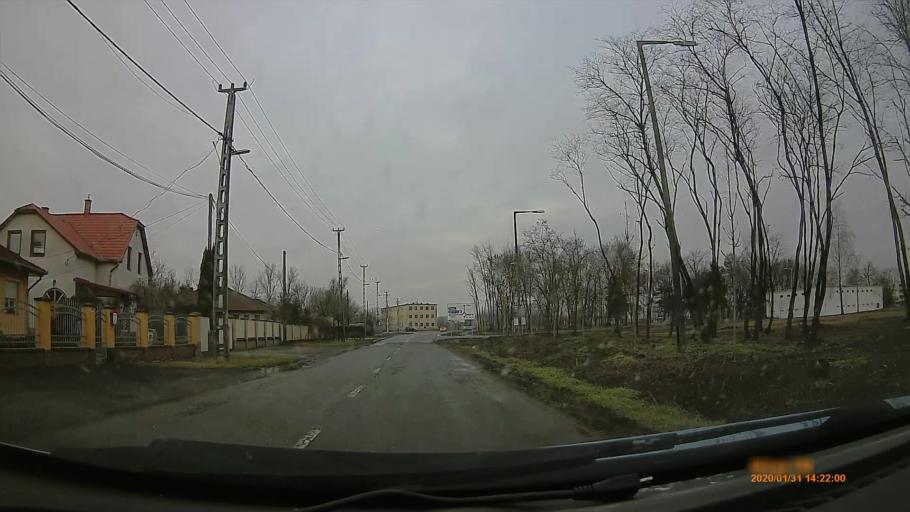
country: HU
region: Szabolcs-Szatmar-Bereg
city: Nyiregyhaza
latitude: 47.9550
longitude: 21.6767
